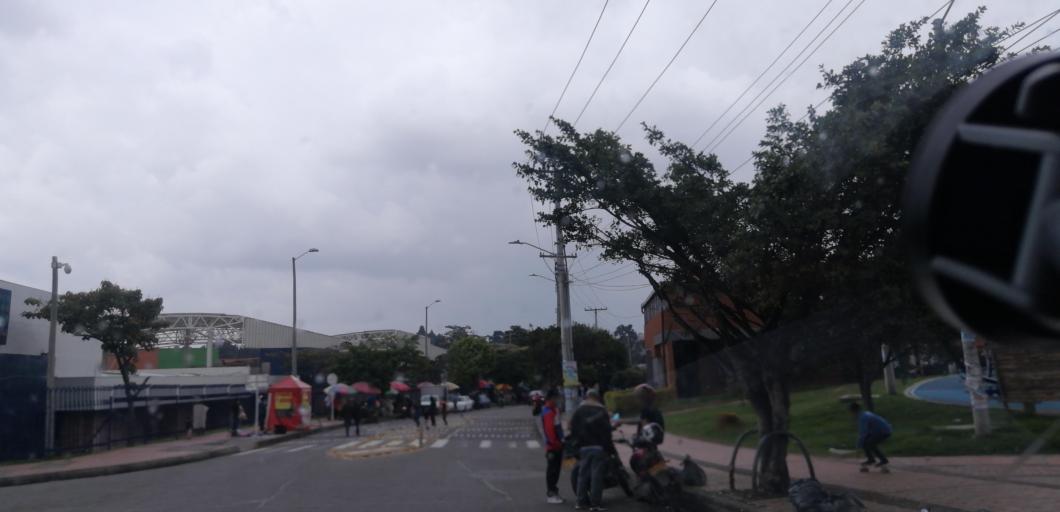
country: CO
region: Bogota D.C.
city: Bogota
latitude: 4.5310
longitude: -74.1176
